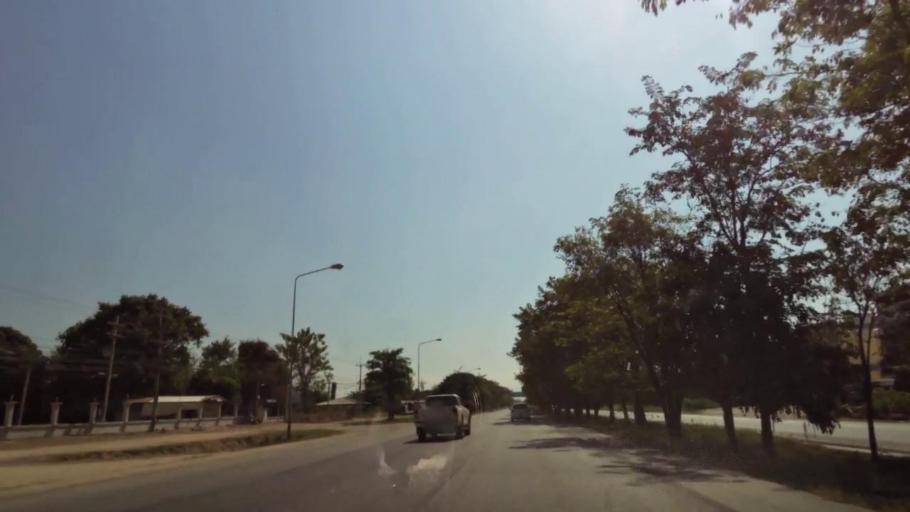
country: TH
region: Nakhon Sawan
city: Kao Liao
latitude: 15.8690
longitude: 100.1166
